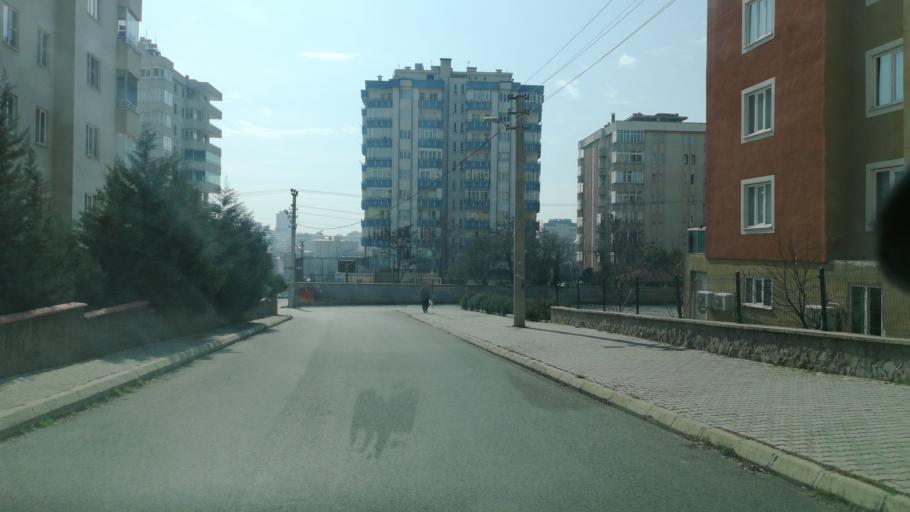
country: TR
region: Kahramanmaras
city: Kahramanmaras
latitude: 37.5880
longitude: 36.8984
